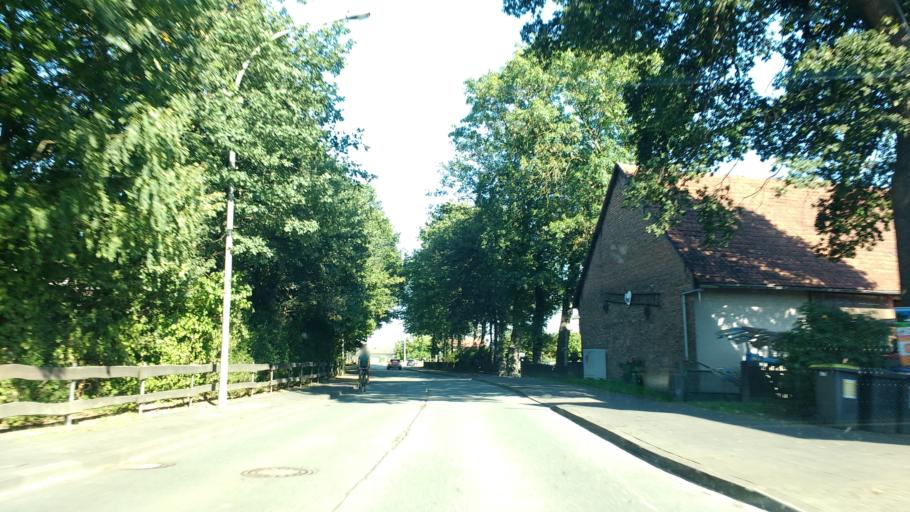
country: DE
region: North Rhine-Westphalia
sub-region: Regierungsbezirk Detmold
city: Hovelhof
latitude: 51.7395
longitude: 8.6654
